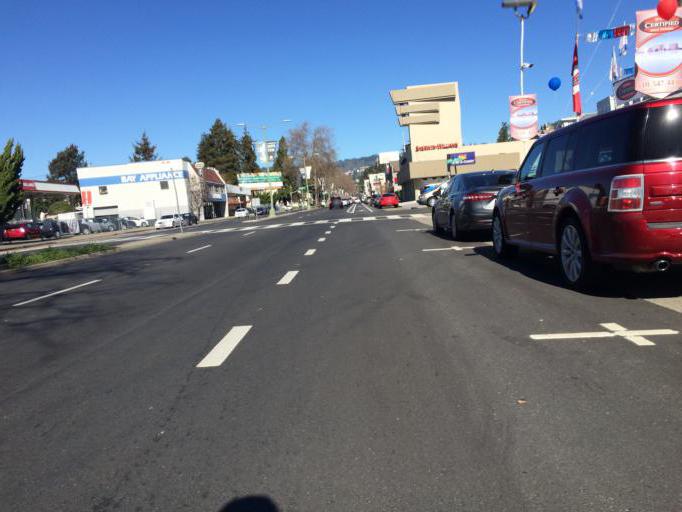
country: US
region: California
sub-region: Alameda County
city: Piedmont
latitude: 37.8295
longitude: -122.2554
